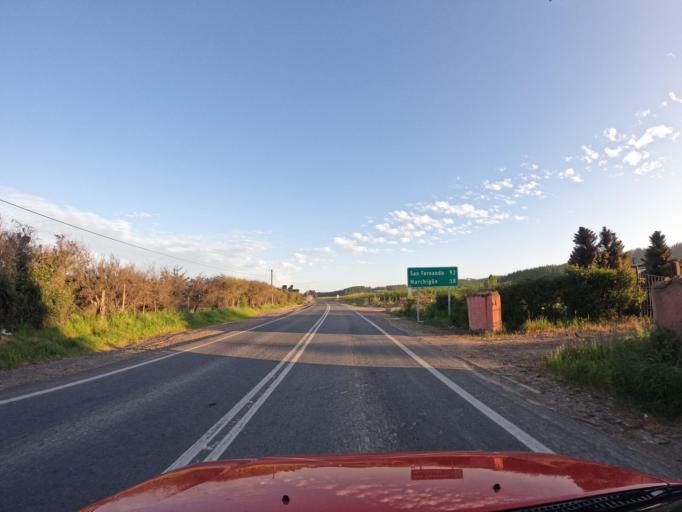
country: CL
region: O'Higgins
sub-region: Provincia de Colchagua
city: Santa Cruz
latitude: -34.3343
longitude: -71.7463
